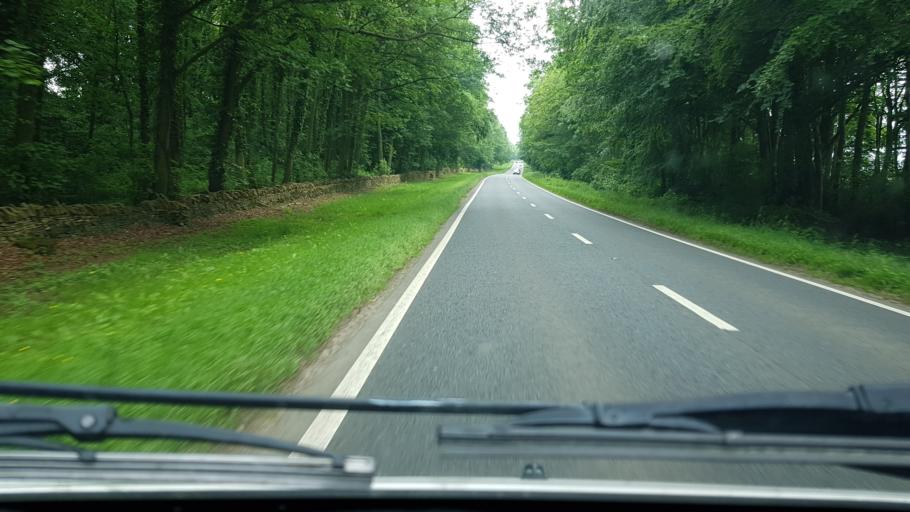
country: GB
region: England
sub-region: Gloucestershire
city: Chipping Campden
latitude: 52.0115
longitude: -1.7957
